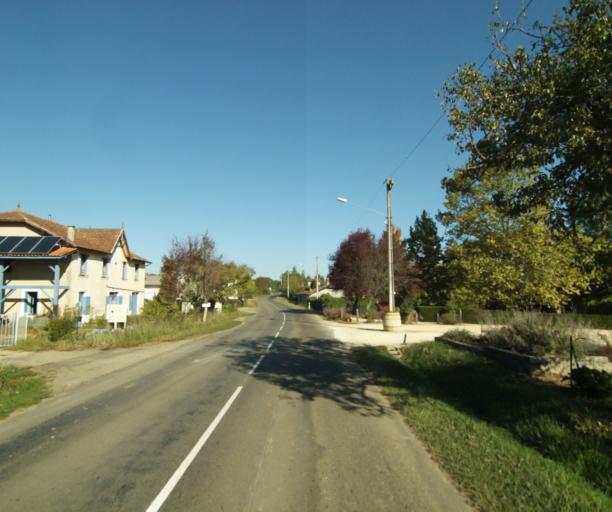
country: FR
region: Aquitaine
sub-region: Departement des Landes
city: Gabarret
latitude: 43.9432
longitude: 0.0143
